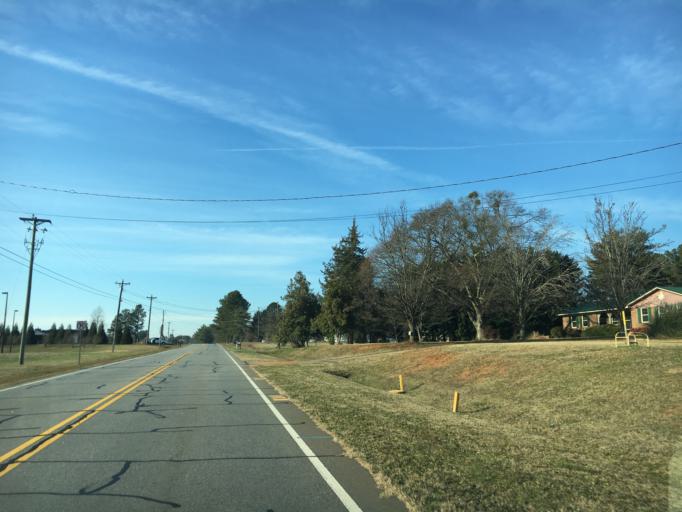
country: US
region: Georgia
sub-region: Hart County
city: Hartwell
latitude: 34.3753
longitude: -83.0007
